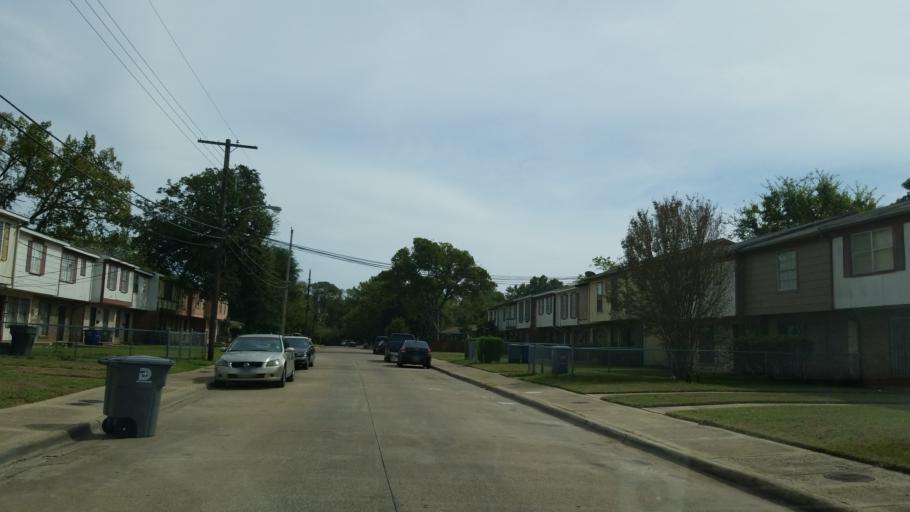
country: US
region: Texas
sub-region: Dallas County
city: Dallas
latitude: 32.7627
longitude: -96.7365
